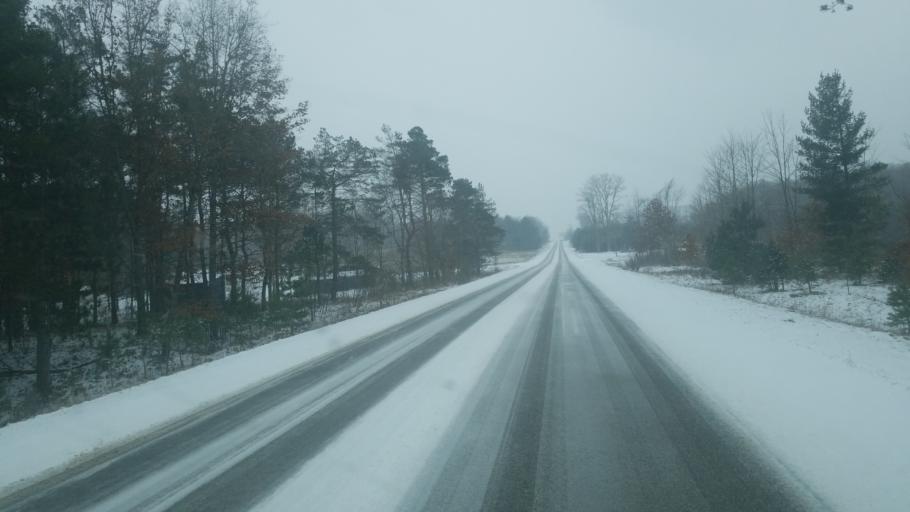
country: US
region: Michigan
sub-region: Osceola County
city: Evart
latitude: 43.8663
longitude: -85.3546
